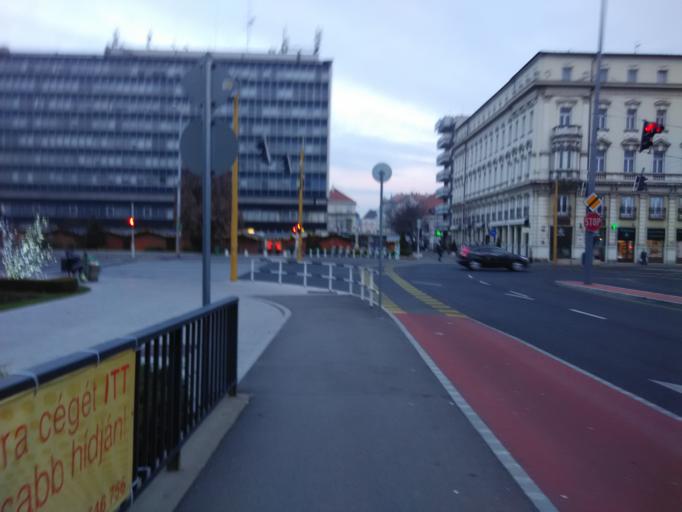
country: HU
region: Gyor-Moson-Sopron
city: Gyor
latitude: 47.6837
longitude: 17.6357
